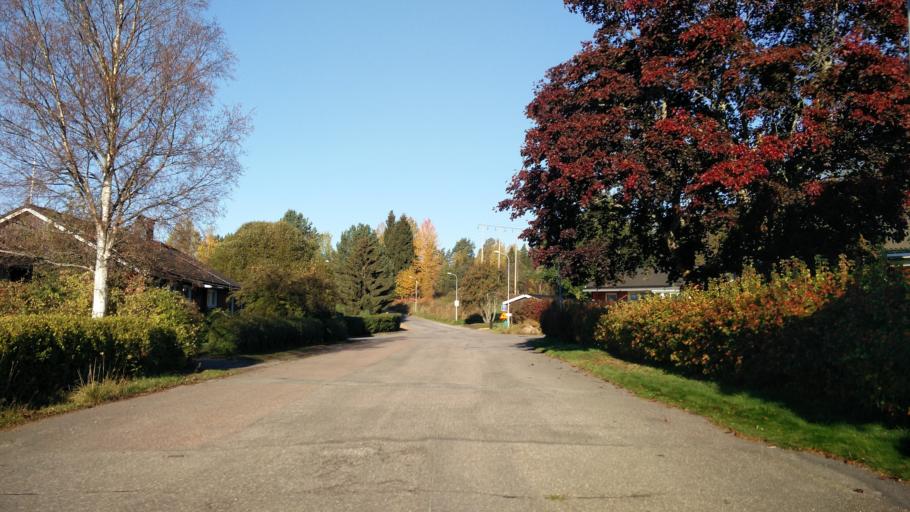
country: SE
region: Vaesternorrland
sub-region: Sundsvalls Kommun
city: Sundsvall
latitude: 62.4068
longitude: 17.2631
